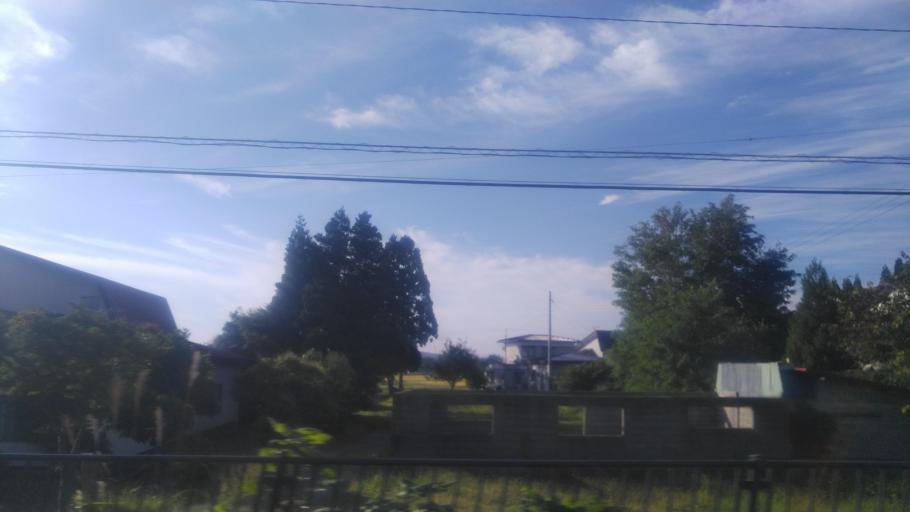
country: JP
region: Akita
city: Takanosu
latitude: 40.2552
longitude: 140.3929
